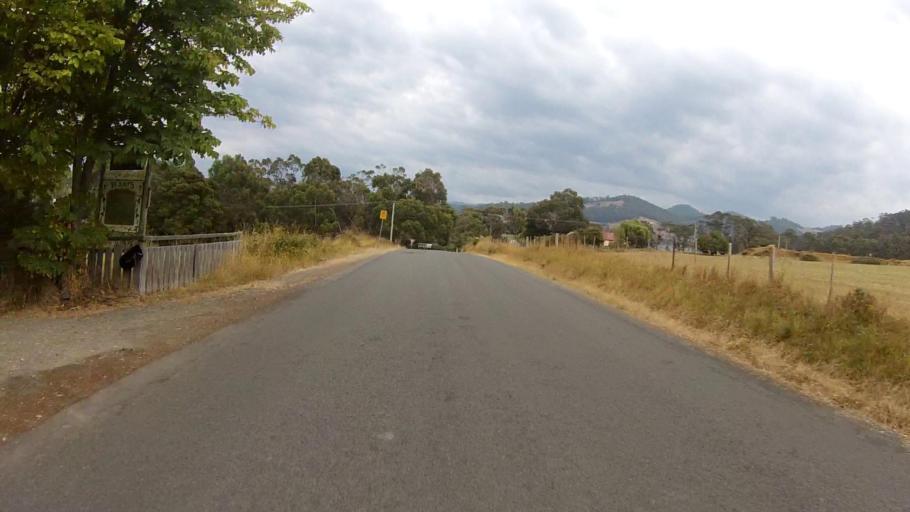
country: AU
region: Tasmania
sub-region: Huon Valley
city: Cygnet
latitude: -43.1840
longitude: 147.1087
